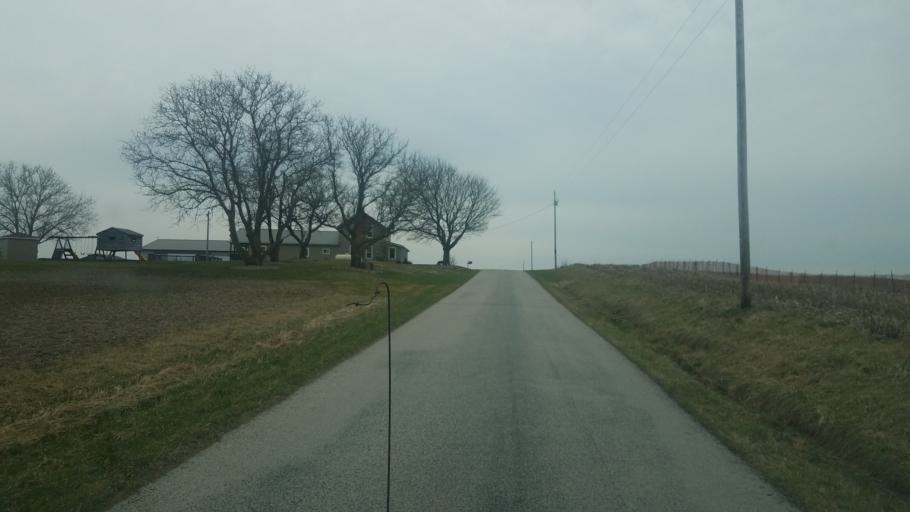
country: US
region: Ohio
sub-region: Huron County
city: Greenwich
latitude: 41.1102
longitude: -82.5639
